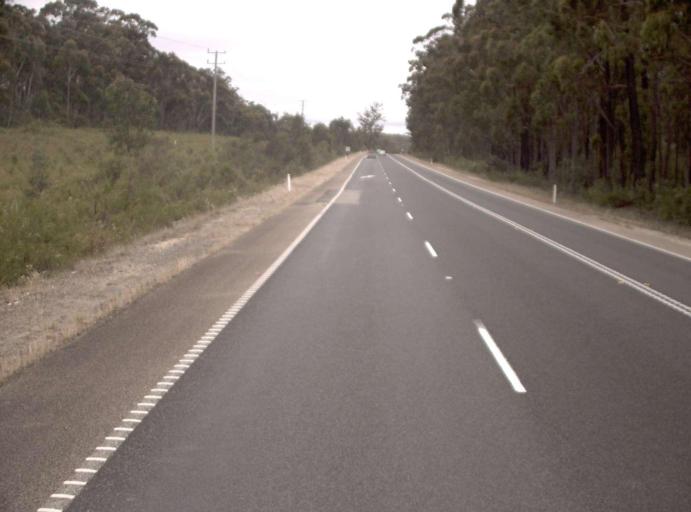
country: AU
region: Victoria
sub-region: East Gippsland
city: Lakes Entrance
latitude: -37.6903
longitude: 148.0265
